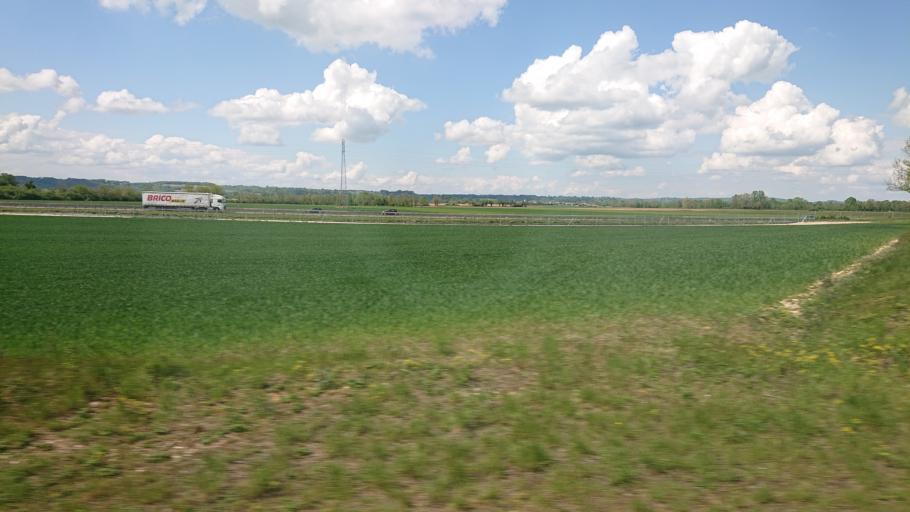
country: FR
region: Rhone-Alpes
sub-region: Departement de l'Ain
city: Leyment
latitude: 45.9381
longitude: 5.2889
